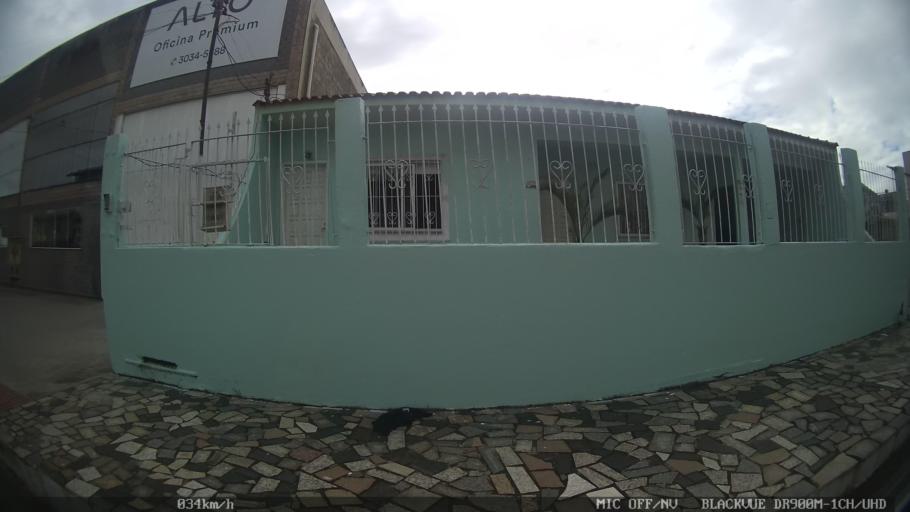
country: BR
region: Santa Catarina
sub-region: Sao Jose
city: Campinas
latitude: -27.5490
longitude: -48.6227
